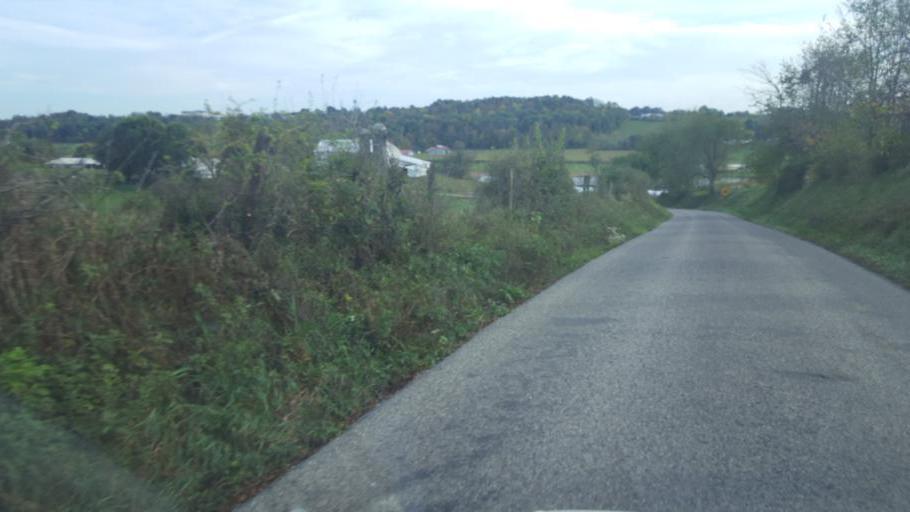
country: US
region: Ohio
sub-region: Holmes County
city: Millersburg
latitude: 40.5749
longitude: -81.8074
